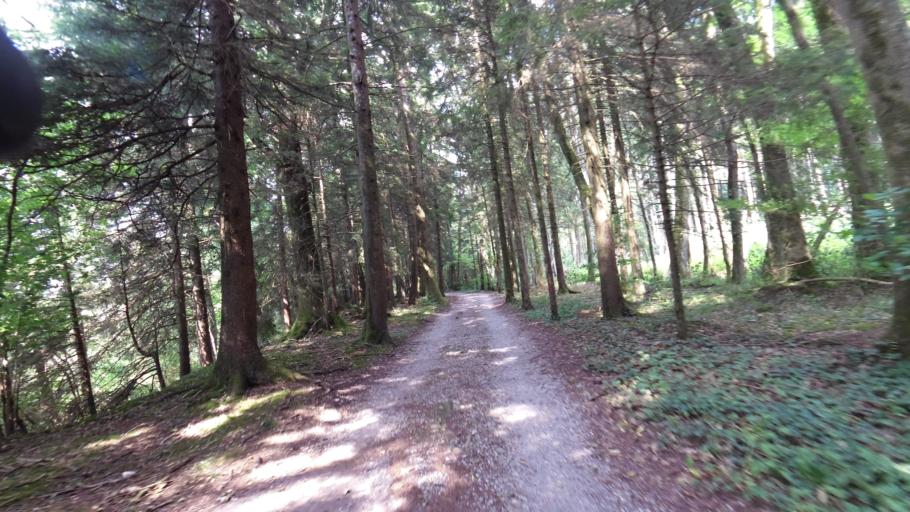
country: DE
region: Bavaria
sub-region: Upper Bavaria
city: Chieming
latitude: 47.8695
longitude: 12.5212
